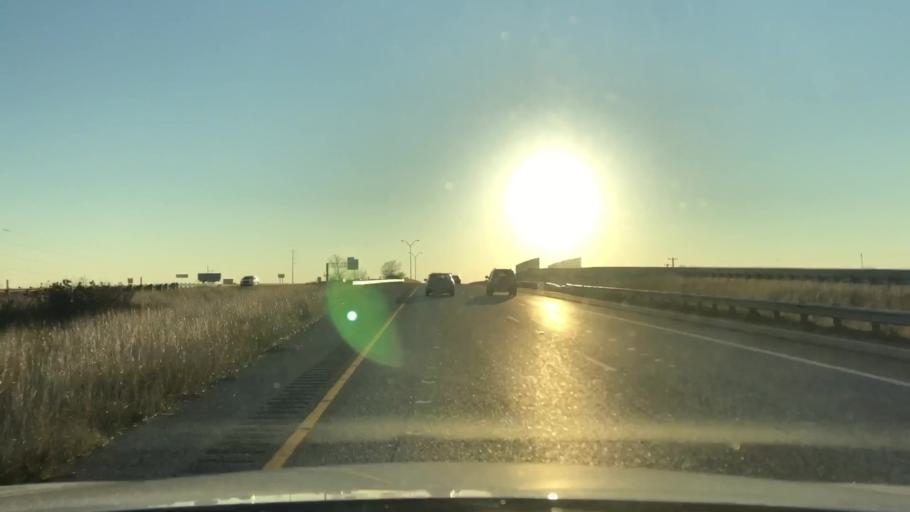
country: US
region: Texas
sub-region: Guadalupe County
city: Seguin
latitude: 29.5885
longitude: -97.9874
